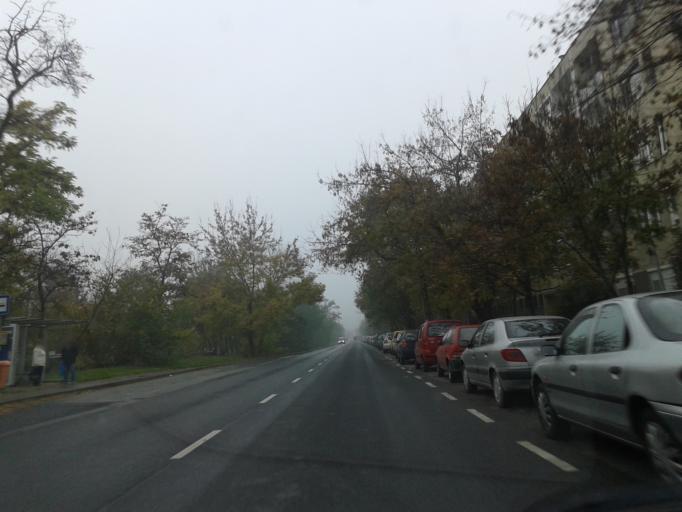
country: HU
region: Pest
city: Halasztelek
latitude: 47.3971
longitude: 18.9982
